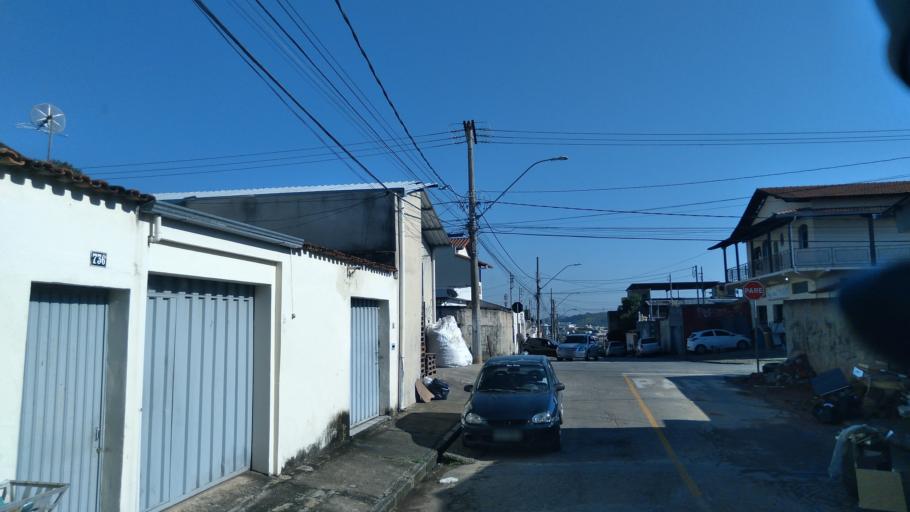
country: BR
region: Minas Gerais
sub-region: Contagem
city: Contagem
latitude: -19.8960
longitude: -44.0206
